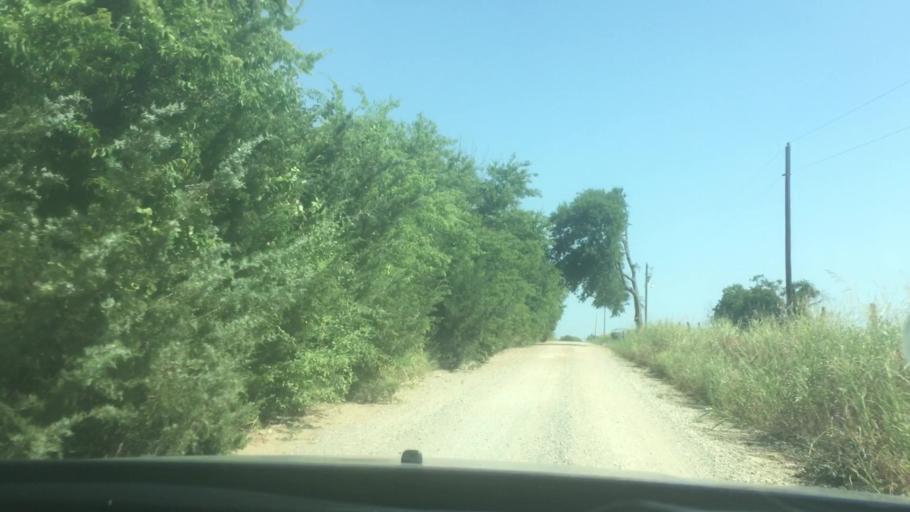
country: US
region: Oklahoma
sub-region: Bryan County
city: Durant
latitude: 34.1378
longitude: -96.4077
